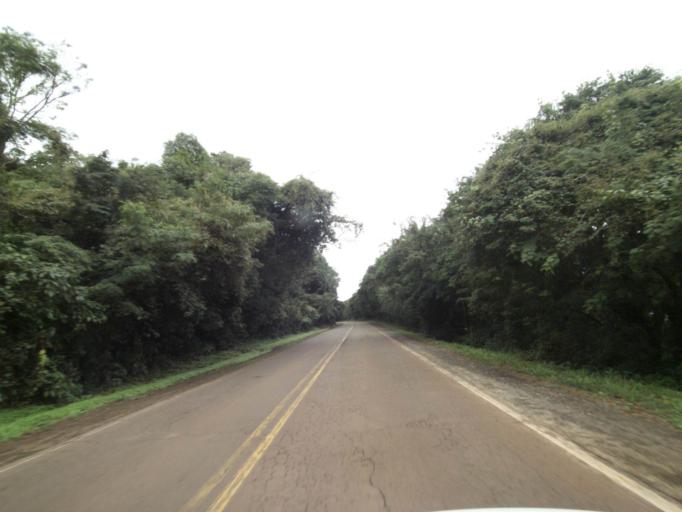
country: BR
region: Parana
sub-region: Marechal Candido Rondon
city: Marechal Candido Rondon
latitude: -24.7974
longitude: -54.2132
